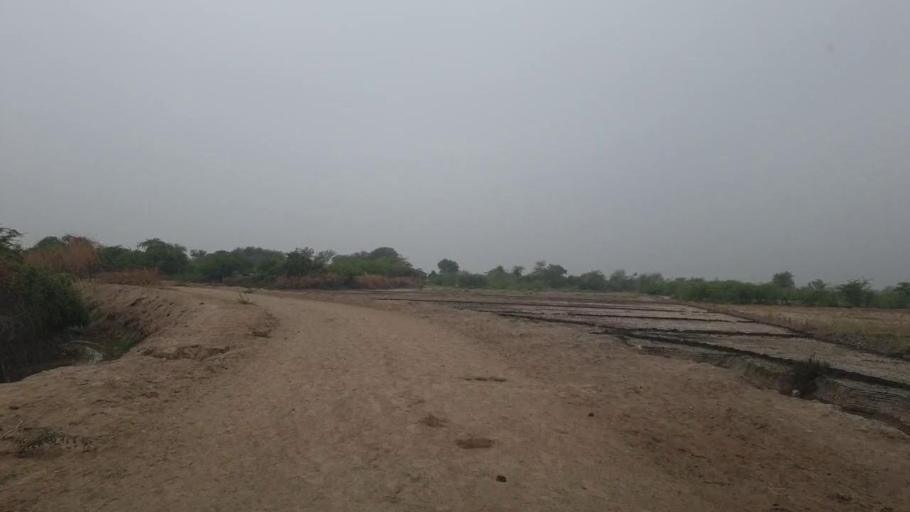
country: PK
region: Sindh
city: Badin
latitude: 24.5687
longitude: 68.6635
